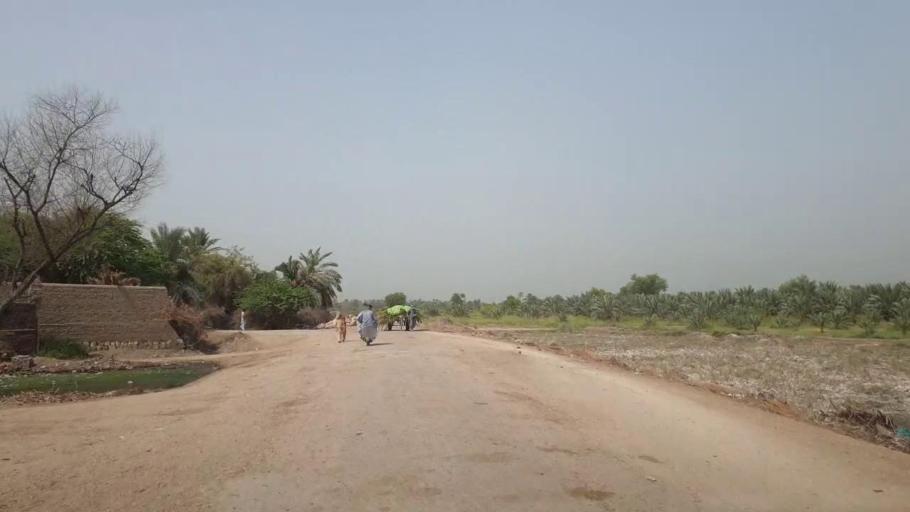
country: PK
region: Sindh
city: Gambat
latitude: 27.4050
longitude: 68.5557
